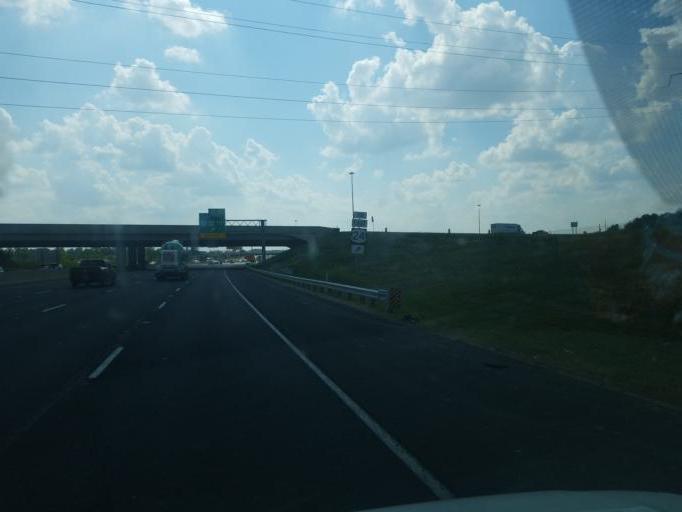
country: US
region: Indiana
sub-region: Allen County
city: Fort Wayne
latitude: 41.1696
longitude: -85.1041
